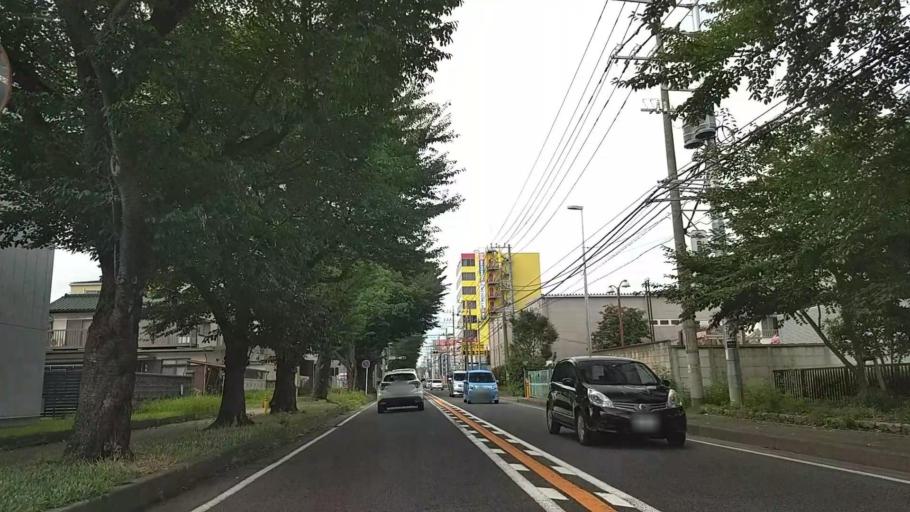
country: JP
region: Kanagawa
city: Minami-rinkan
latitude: 35.4785
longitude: 139.4648
